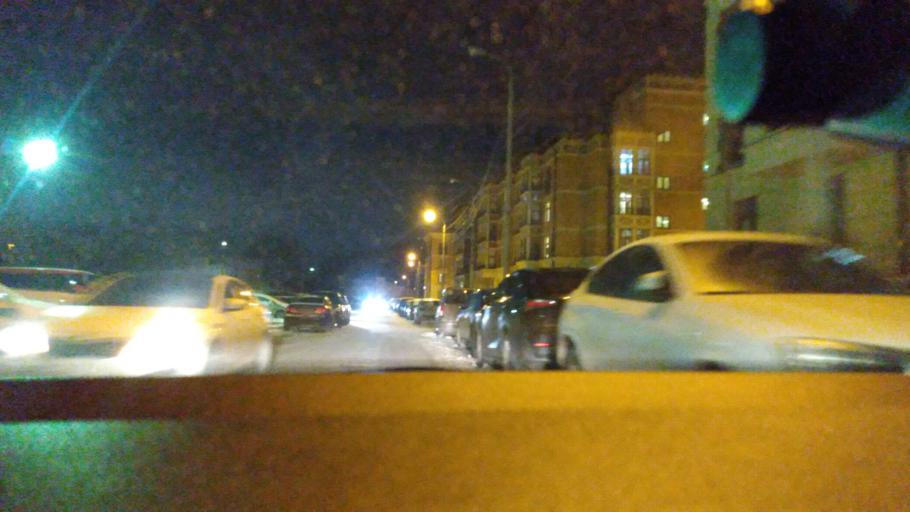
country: RU
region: Moskovskaya
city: Opalikha
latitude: 55.8143
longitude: 37.2471
